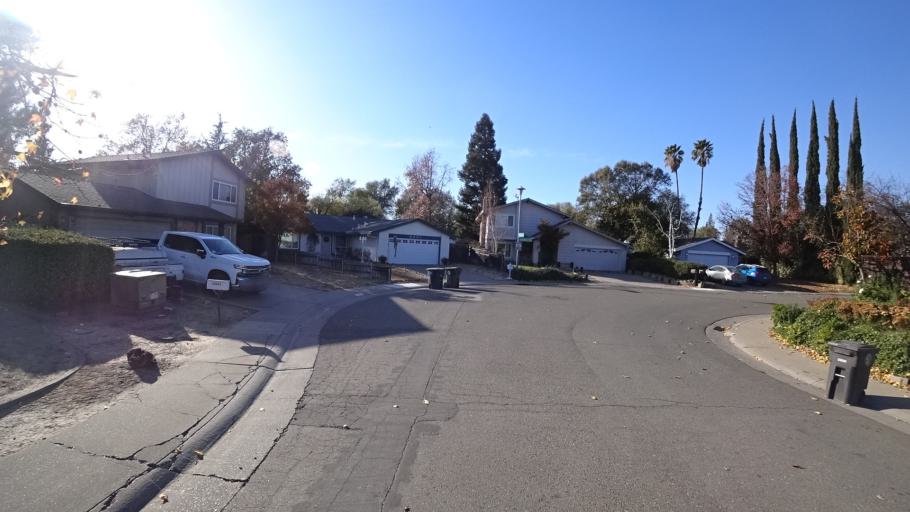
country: US
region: California
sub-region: Sacramento County
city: Antelope
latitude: 38.6930
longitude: -121.3174
